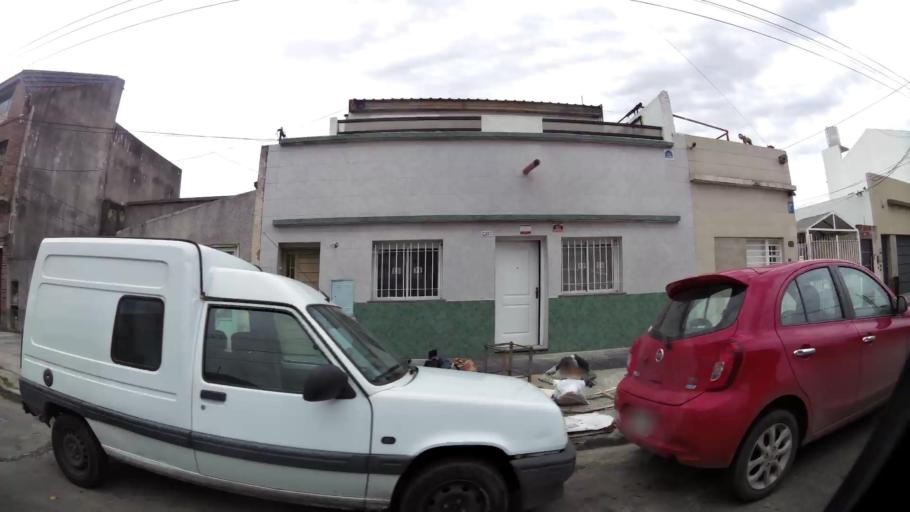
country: AR
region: Buenos Aires
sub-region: Partido de Lanus
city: Lanus
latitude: -34.6816
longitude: -58.3986
